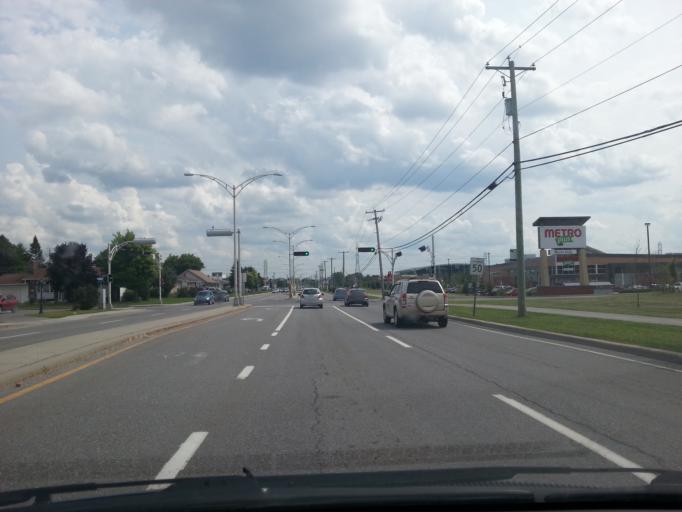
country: CA
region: Quebec
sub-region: Outaouais
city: Gatineau
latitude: 45.4933
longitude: -75.6757
